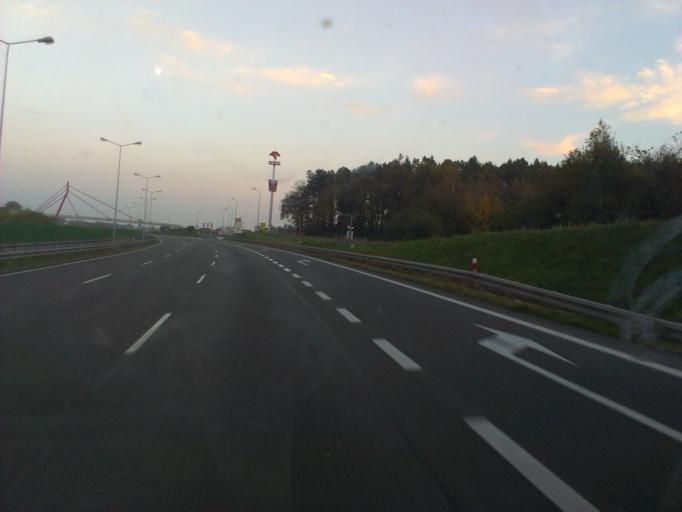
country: PL
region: Opole Voivodeship
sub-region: Powiat strzelecki
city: Lesnica
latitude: 50.4626
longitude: 18.1571
